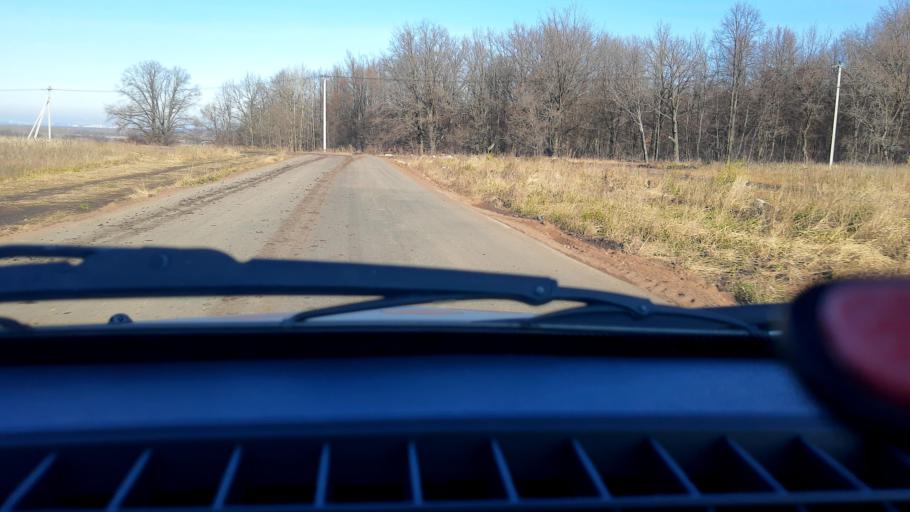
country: RU
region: Bashkortostan
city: Kabakovo
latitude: 54.6211
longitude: 56.1538
